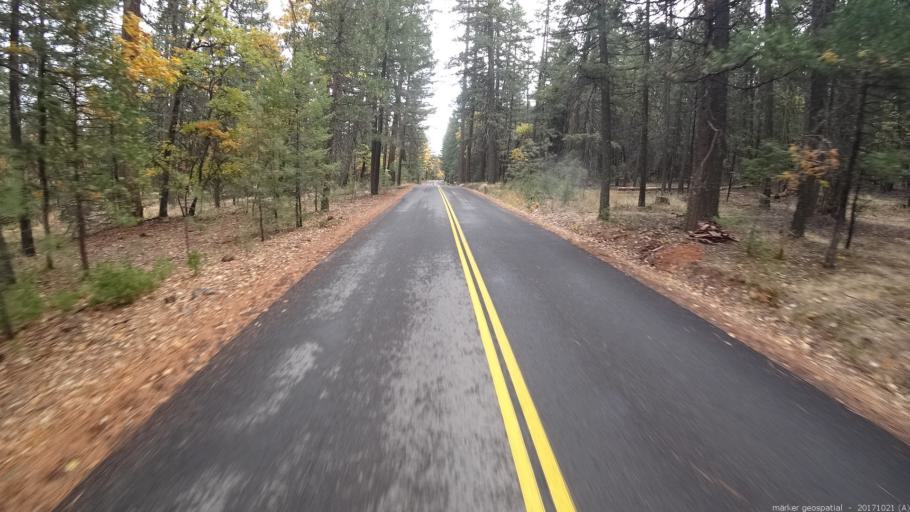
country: US
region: California
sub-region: Shasta County
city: Burney
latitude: 41.0167
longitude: -121.6589
